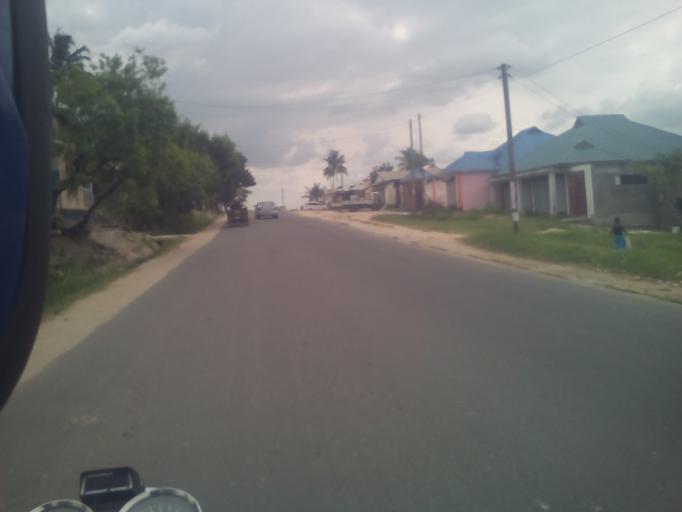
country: TZ
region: Dar es Salaam
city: Dar es Salaam
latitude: -6.8697
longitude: 39.2226
